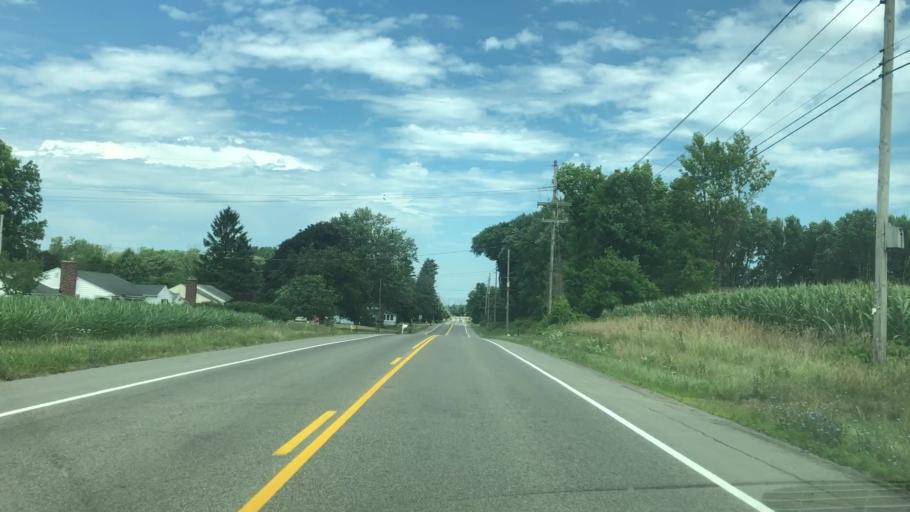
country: US
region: New York
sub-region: Monroe County
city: Webster
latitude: 43.2109
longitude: -77.4004
